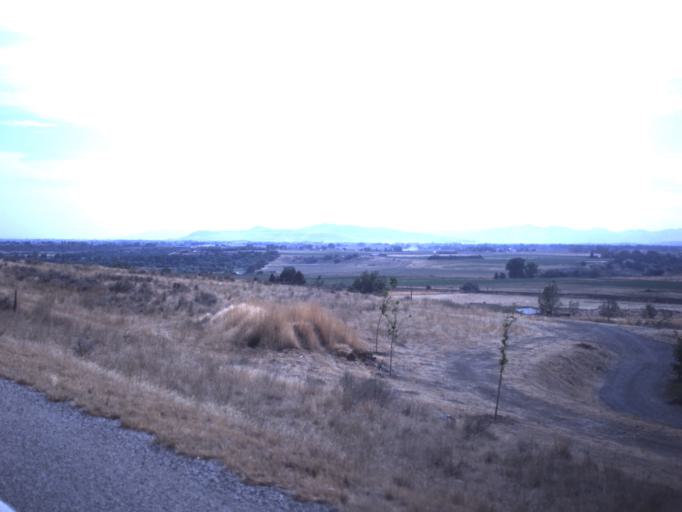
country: US
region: Utah
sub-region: Box Elder County
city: Garland
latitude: 41.7400
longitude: -112.0985
